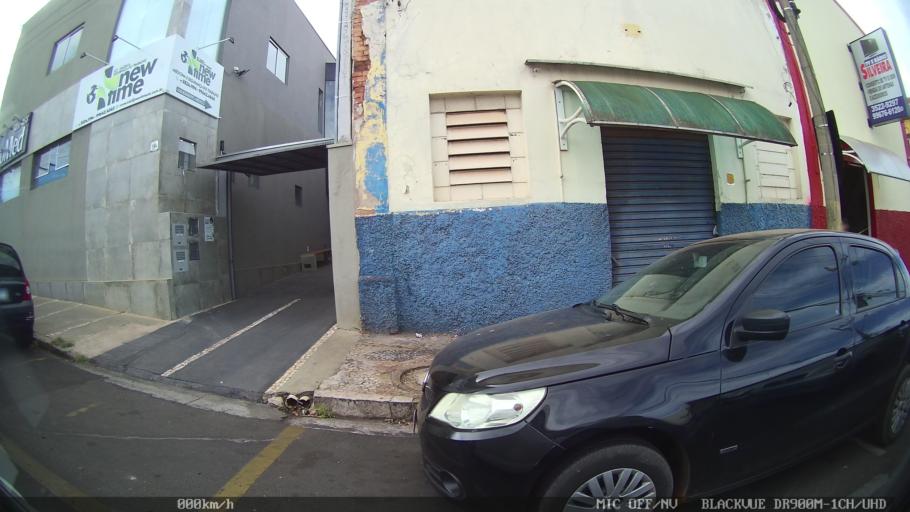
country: BR
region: Sao Paulo
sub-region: Catanduva
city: Catanduva
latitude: -21.1297
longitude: -48.9684
